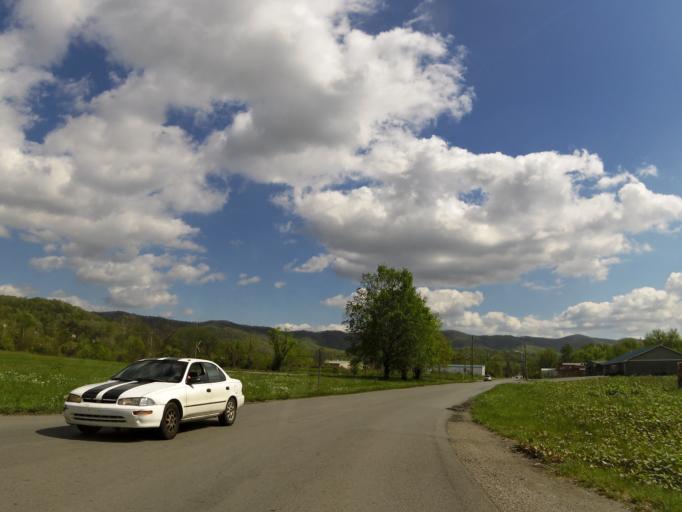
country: US
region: Kentucky
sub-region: Bell County
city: Middlesboro
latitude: 36.6170
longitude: -83.7076
